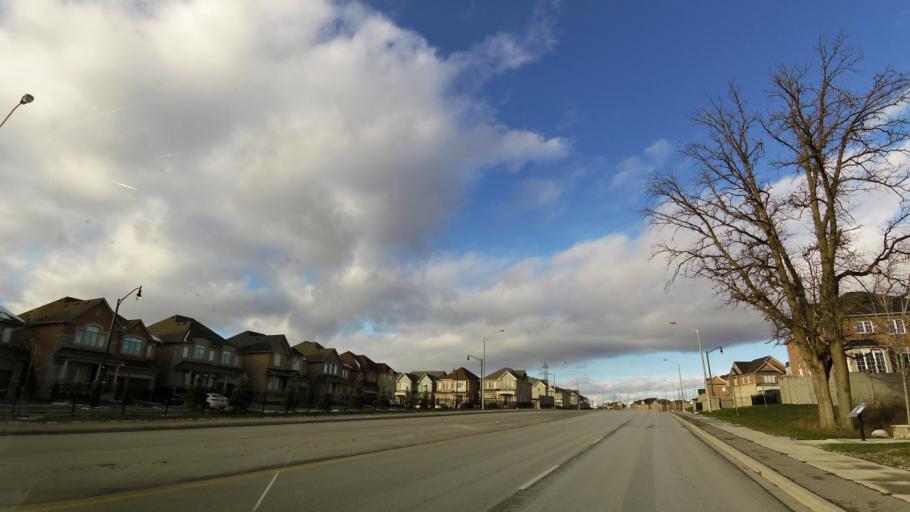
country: CA
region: Ontario
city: Brampton
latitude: 43.6580
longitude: -79.7824
